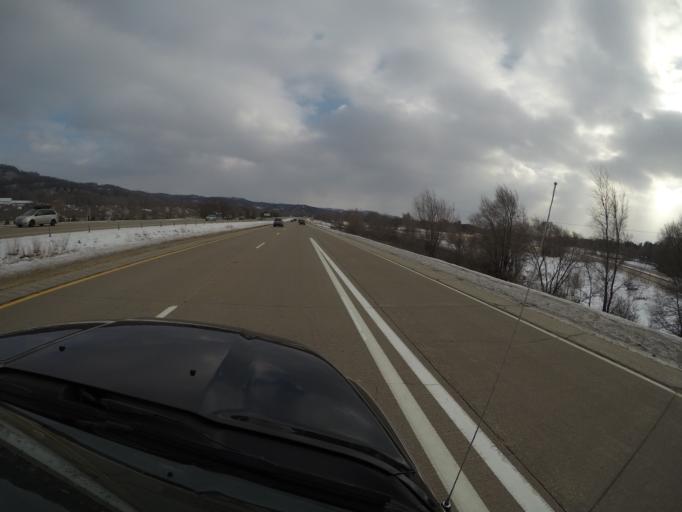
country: US
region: Wisconsin
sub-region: La Crosse County
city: Holmen
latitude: 43.9414
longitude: -91.2558
